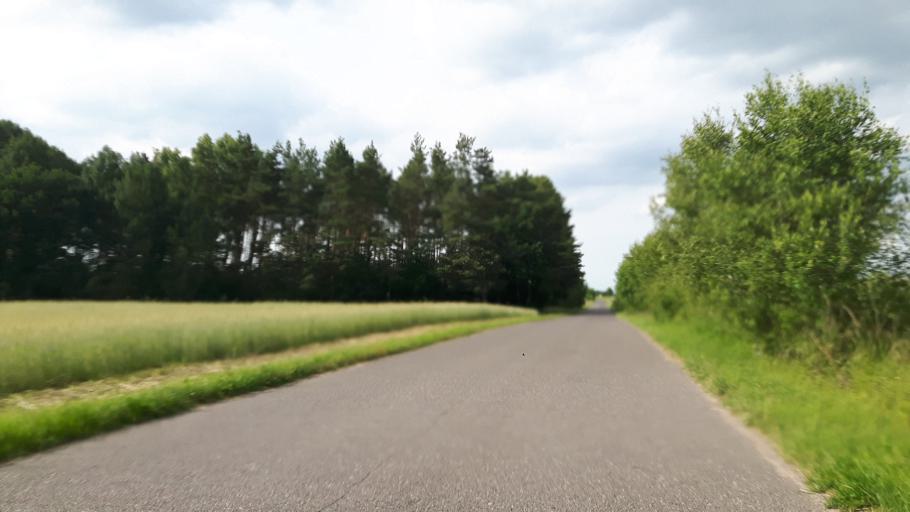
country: PL
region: West Pomeranian Voivodeship
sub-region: Powiat gryficki
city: Gryfice
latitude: 53.8073
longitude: 15.1282
